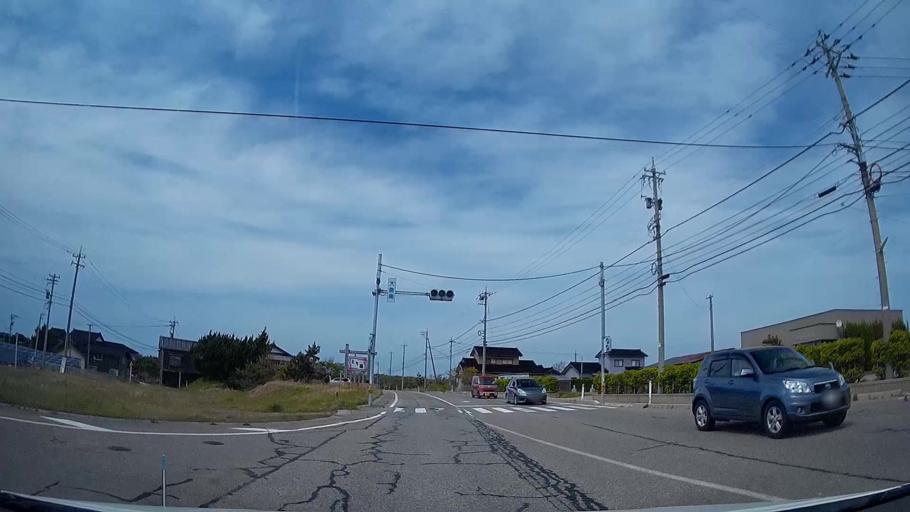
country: JP
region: Ishikawa
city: Hakui
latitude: 36.9788
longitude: 136.7766
